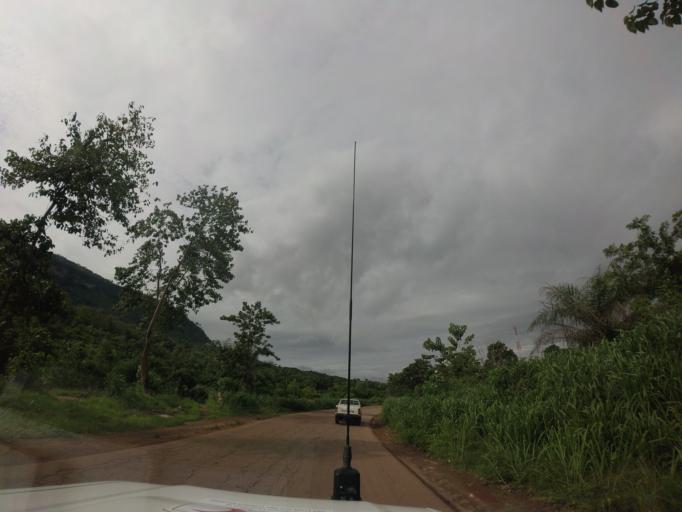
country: GN
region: Kindia
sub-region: Coyah
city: Coyah
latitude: 9.7247
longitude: -13.3709
